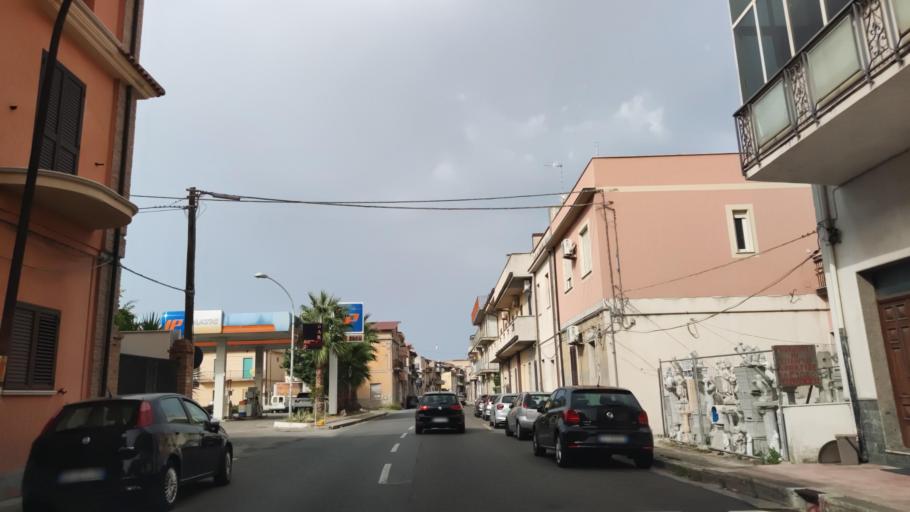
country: IT
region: Calabria
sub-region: Provincia di Reggio Calabria
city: Siderno
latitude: 38.2606
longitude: 16.2880
